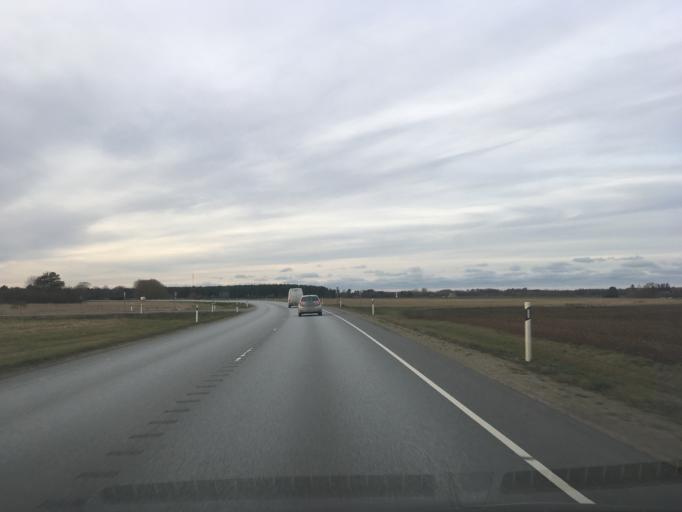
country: EE
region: Ida-Virumaa
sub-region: Puessi linn
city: Pussi
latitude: 59.4105
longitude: 27.0472
